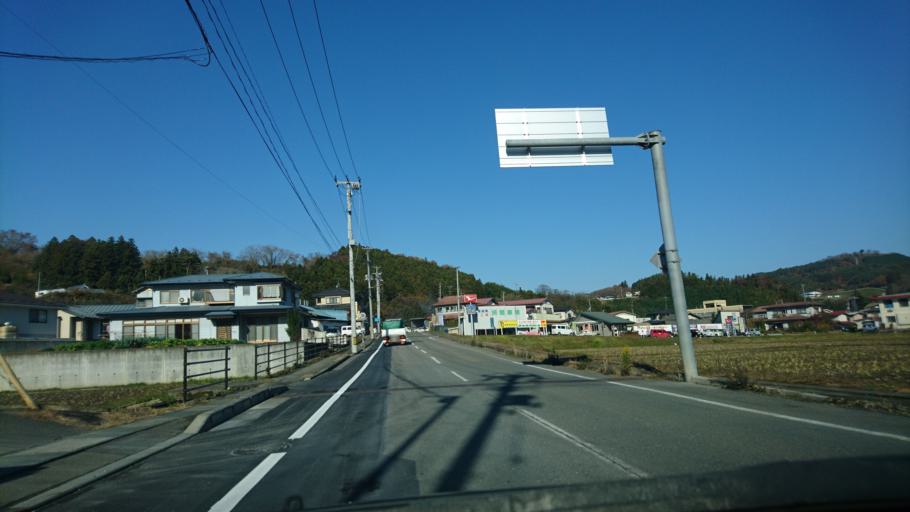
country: JP
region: Iwate
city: Ichinoseki
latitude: 38.9885
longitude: 141.2505
